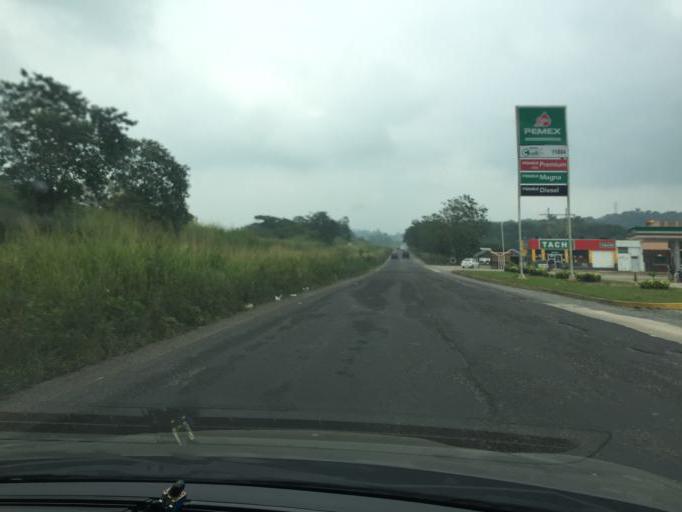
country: MX
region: Veracruz
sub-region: Moloacan
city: Tlacuilolapan
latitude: 18.0731
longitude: -94.2879
